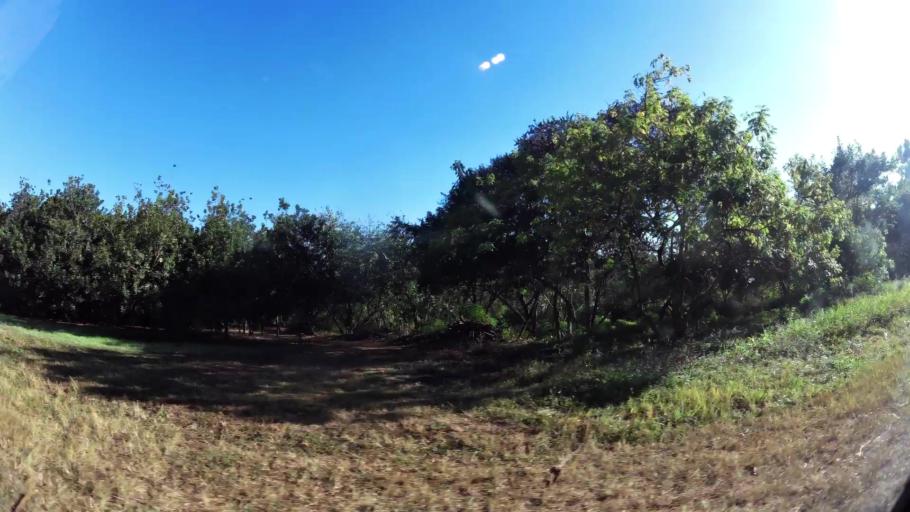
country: ZA
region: Limpopo
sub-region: Mopani District Municipality
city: Tzaneen
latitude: -23.8891
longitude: 30.0850
